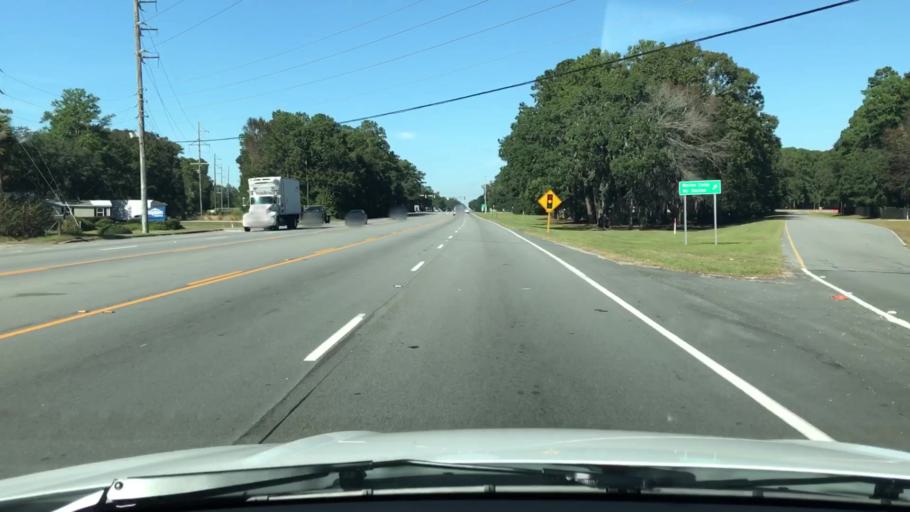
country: US
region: South Carolina
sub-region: Beaufort County
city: Burton
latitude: 32.4549
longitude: -80.7327
